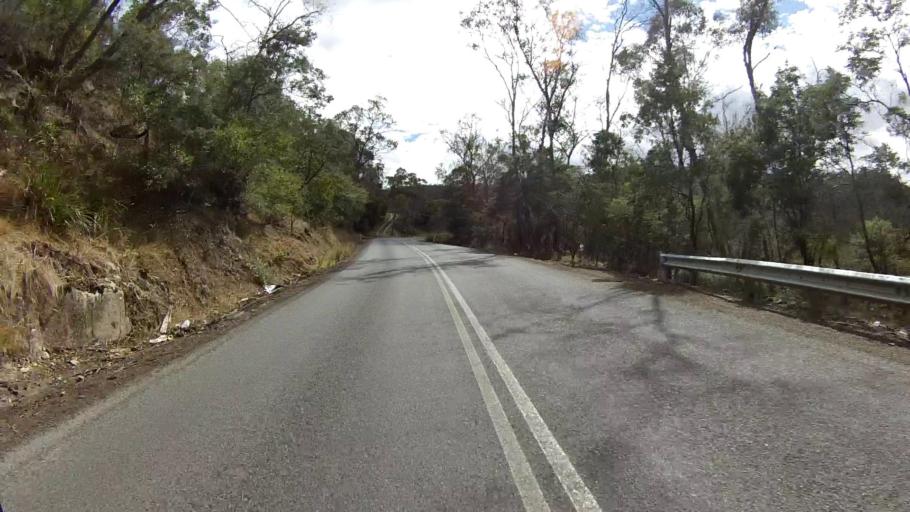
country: AU
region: Tasmania
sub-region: Clarence
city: Lindisfarne
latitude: -42.7910
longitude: 147.3590
